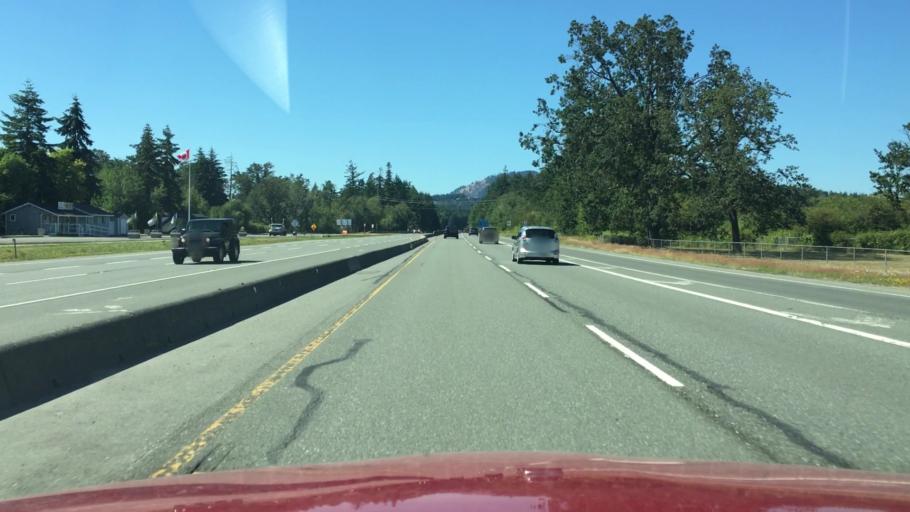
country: CA
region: British Columbia
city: North Saanich
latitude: 48.6639
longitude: -123.4184
